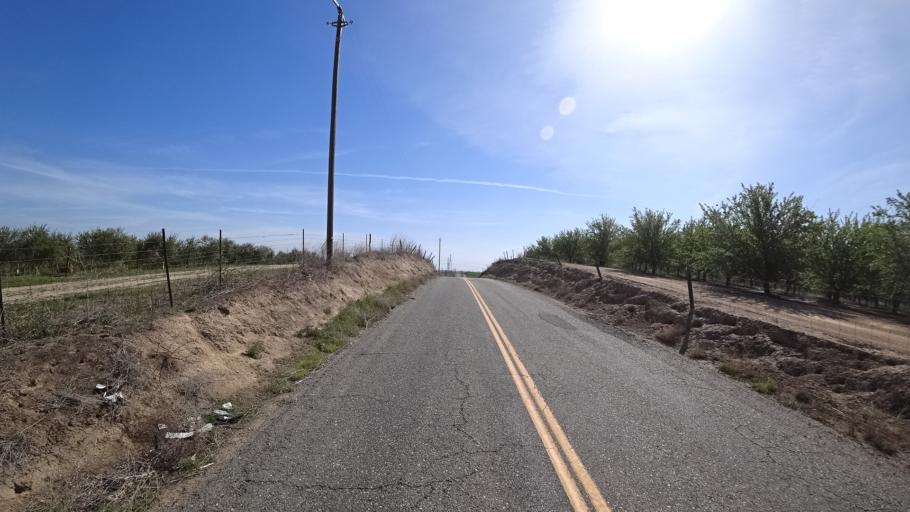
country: US
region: California
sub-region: Glenn County
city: Willows
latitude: 39.6115
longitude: -122.2825
